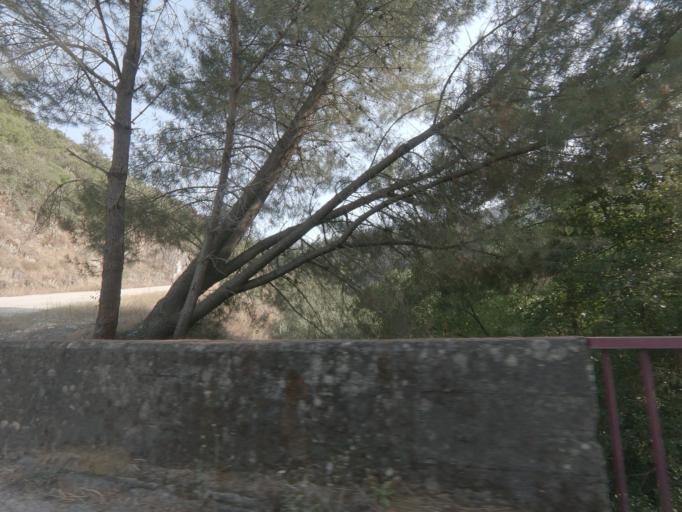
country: PT
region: Viseu
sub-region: Tabuaco
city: Tabuaco
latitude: 41.1276
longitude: -7.5488
